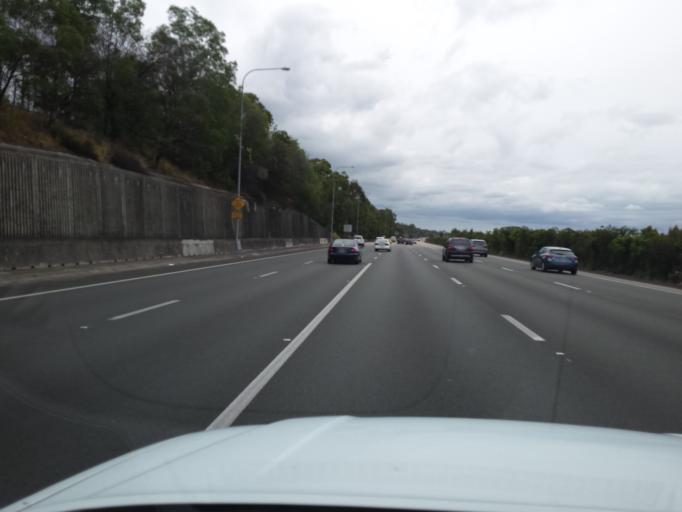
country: AU
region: Queensland
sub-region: Gold Coast
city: Nerang
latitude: -27.9485
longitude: 153.3409
